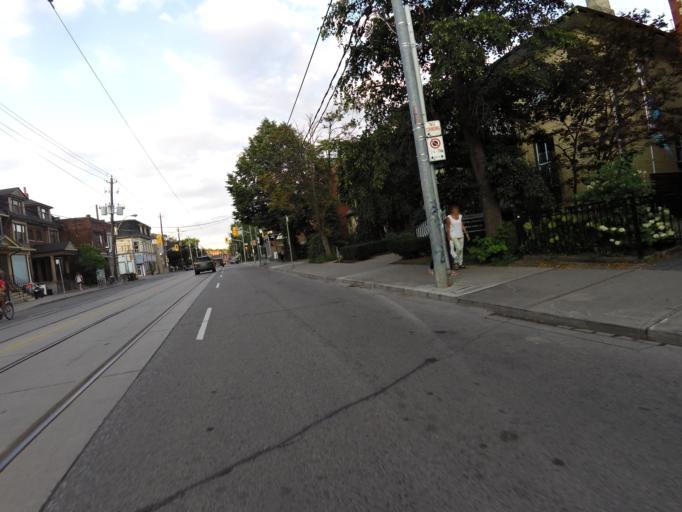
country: CA
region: Ontario
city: Toronto
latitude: 43.6635
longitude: -79.3713
